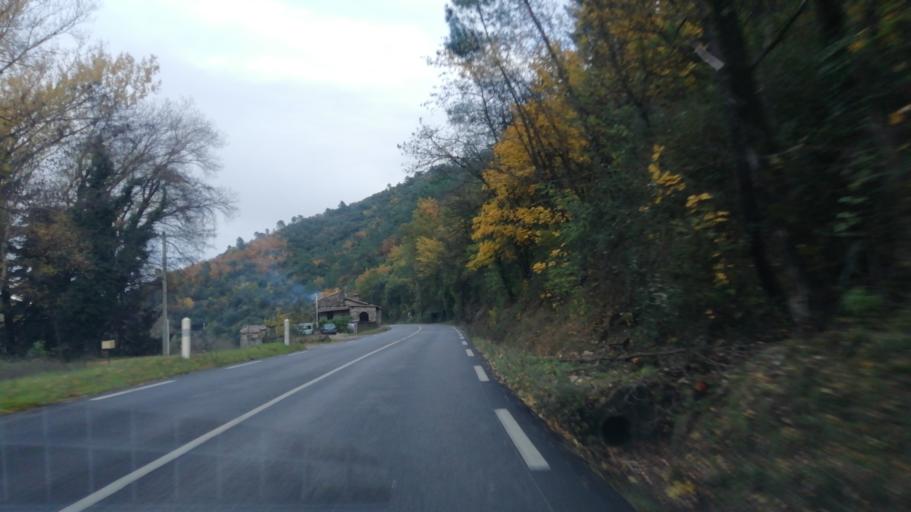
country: FR
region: Languedoc-Roussillon
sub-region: Departement du Gard
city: Anduze
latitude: 44.0723
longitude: 3.9548
